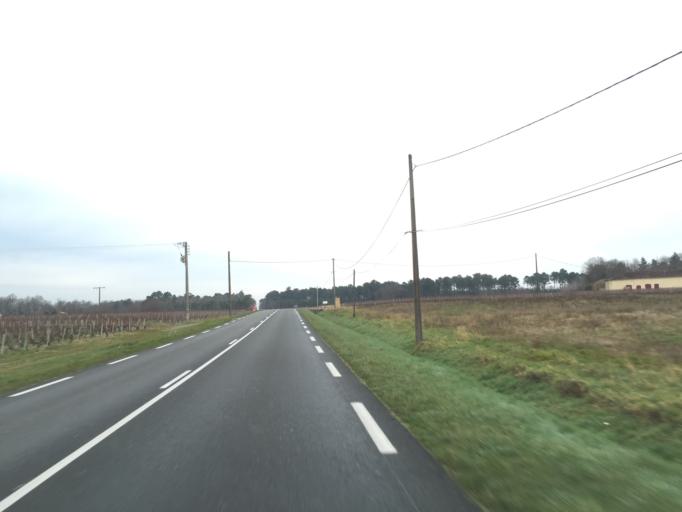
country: FR
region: Aquitaine
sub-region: Departement de la Gironde
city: Saint-Sauveur
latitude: 45.1689
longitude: -0.8344
